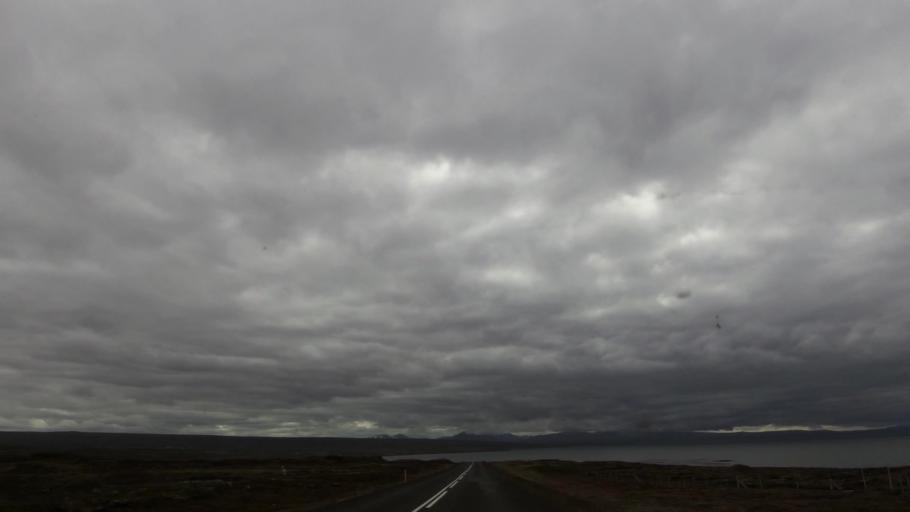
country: IS
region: West
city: Borgarnes
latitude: 65.1869
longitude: -21.7148
